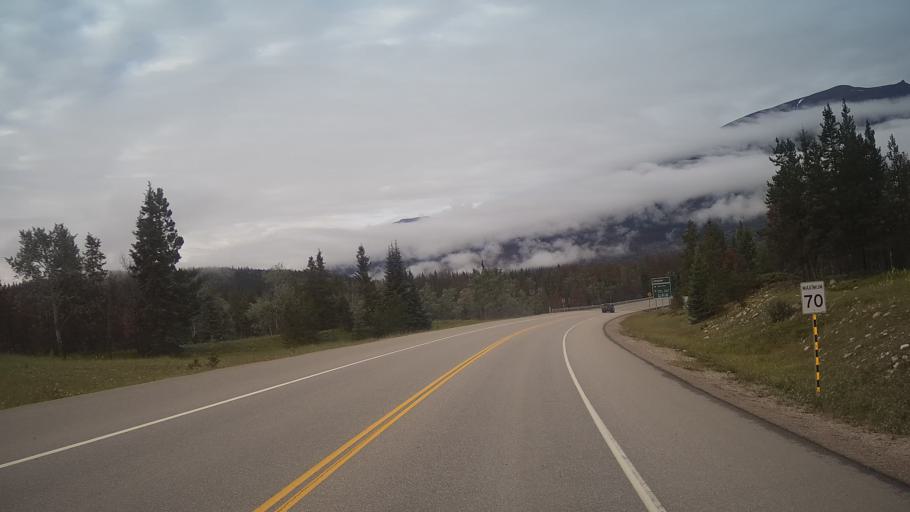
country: CA
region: Alberta
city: Jasper Park Lodge
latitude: 52.8731
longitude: -118.0719
